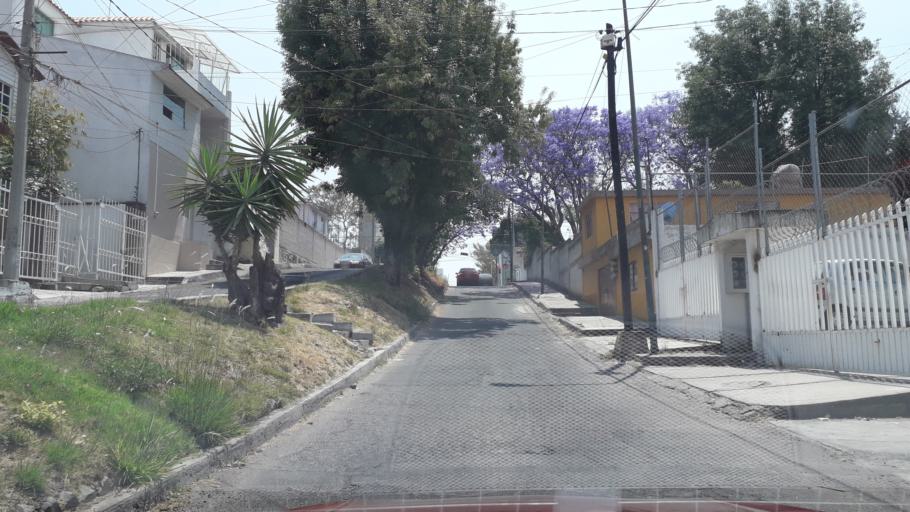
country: MX
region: Puebla
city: Puebla
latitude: 19.0530
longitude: -98.2351
